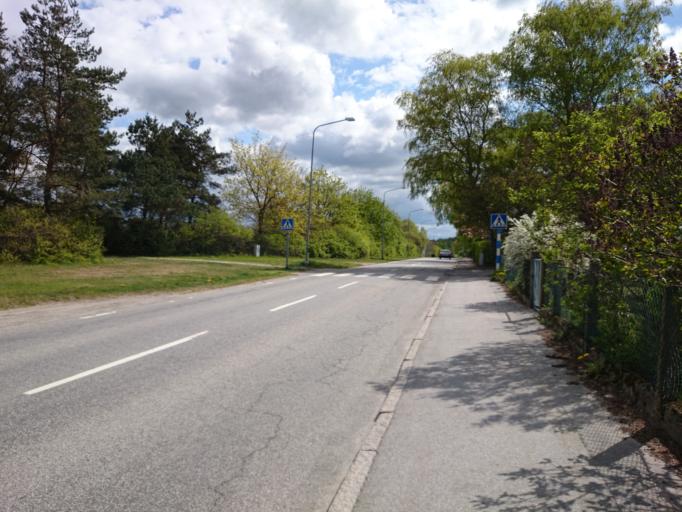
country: SE
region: Skane
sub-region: Lunds Kommun
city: Genarp
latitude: 55.5971
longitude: 13.4084
